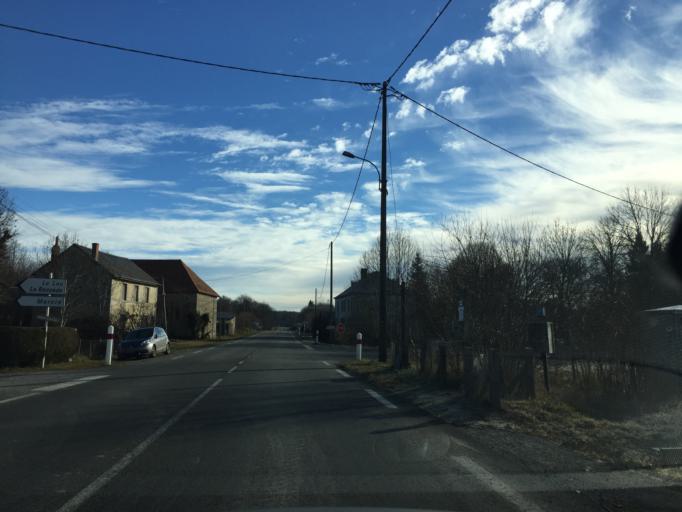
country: FR
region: Limousin
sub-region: Departement de la Creuse
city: Auzances
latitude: 45.8864
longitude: 2.4912
